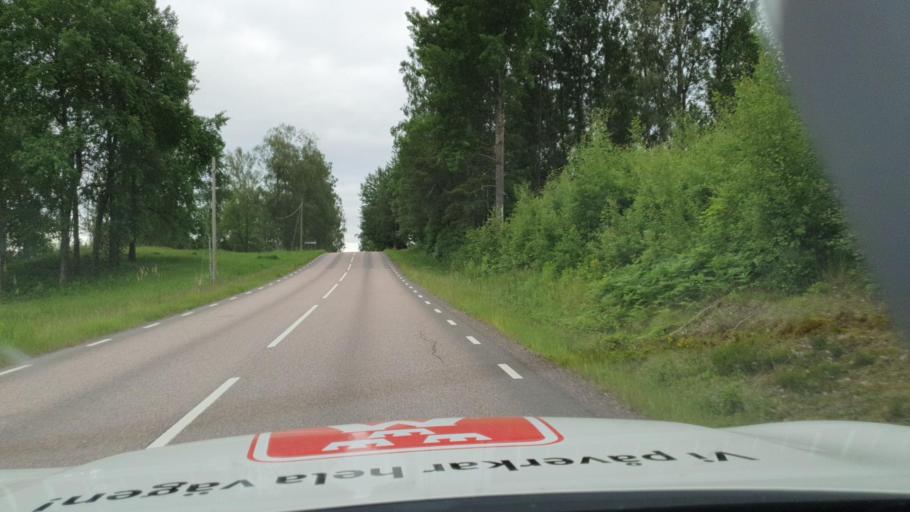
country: SE
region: Vaermland
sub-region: Kils Kommun
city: Kil
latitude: 59.5085
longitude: 13.3904
